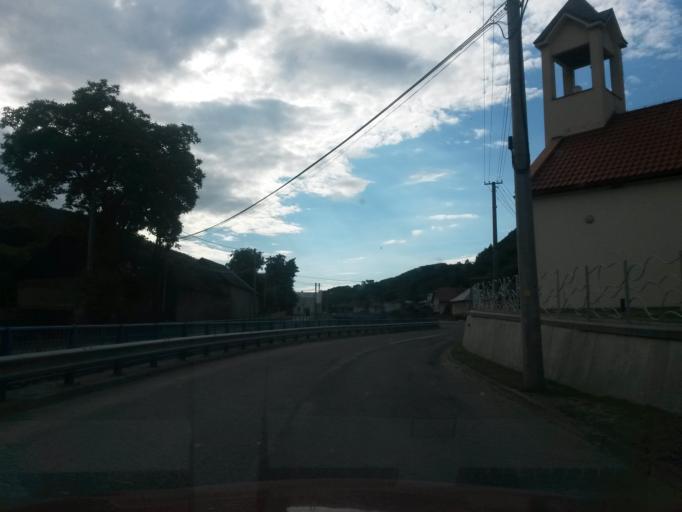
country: SK
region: Presovsky
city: Sabinov
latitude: 49.0862
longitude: 21.0244
